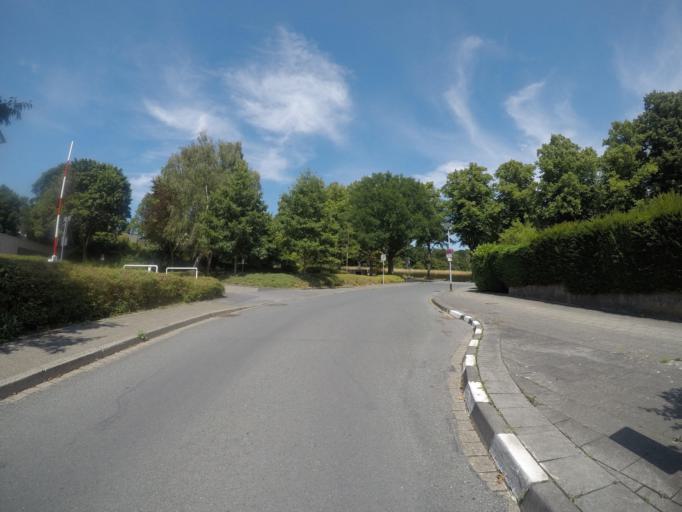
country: DE
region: North Rhine-Westphalia
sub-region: Regierungsbezirk Dusseldorf
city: Kleve
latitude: 51.7818
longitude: 6.1086
